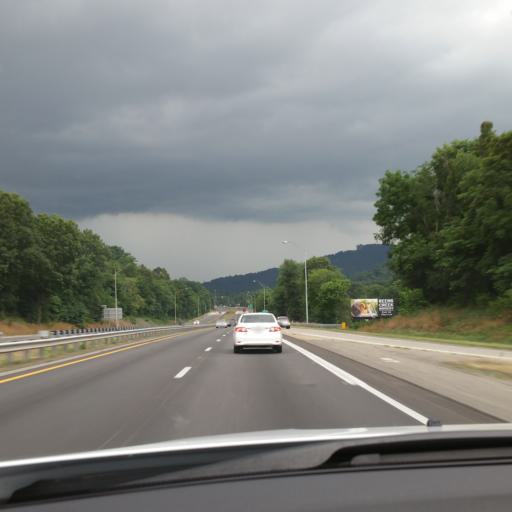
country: US
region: North Carolina
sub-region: Buncombe County
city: Woodfin
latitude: 35.6334
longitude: -82.5806
